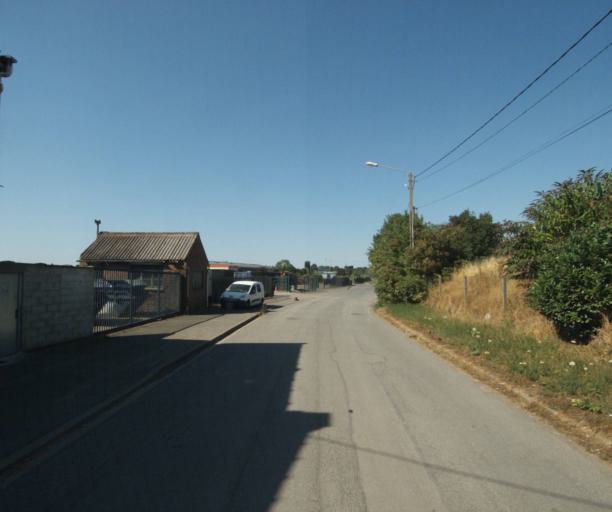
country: FR
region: Nord-Pas-de-Calais
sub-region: Departement du Nord
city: Wervicq-Sud
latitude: 50.7744
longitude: 3.0619
